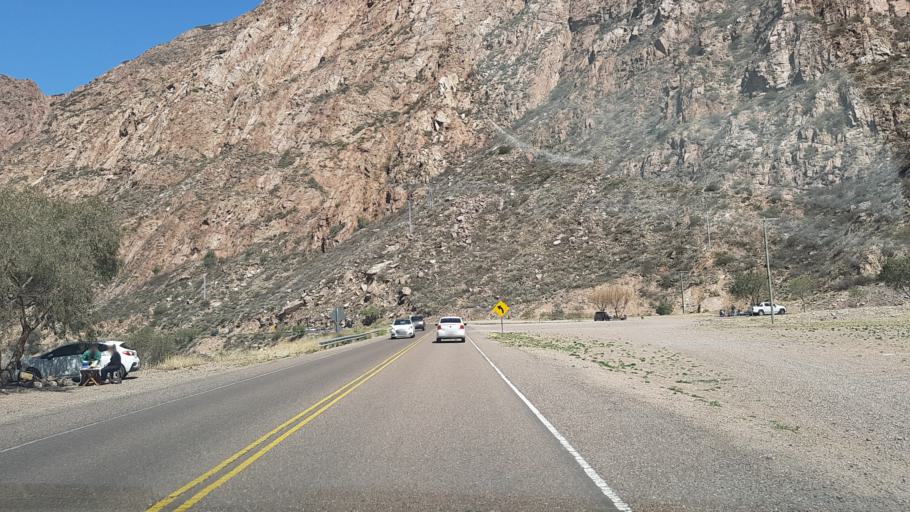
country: AR
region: Mendoza
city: Lujan de Cuyo
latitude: -33.0086
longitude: -69.1223
